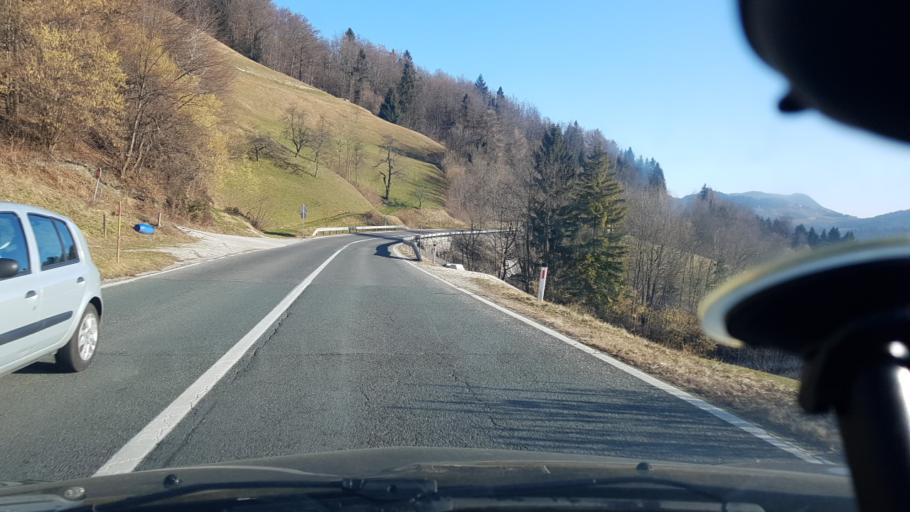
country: SI
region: Zagorje ob Savi
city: Izlake
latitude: 46.1845
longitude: 14.8725
